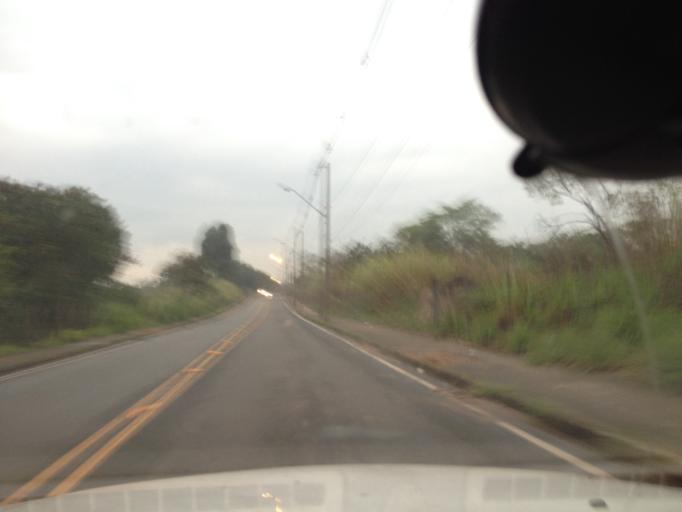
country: BR
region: Sao Paulo
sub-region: Salto
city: Salto
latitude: -23.2020
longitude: -47.2702
